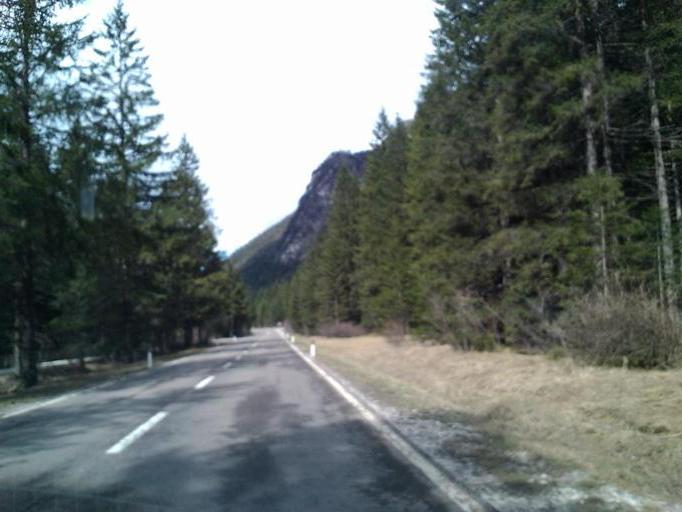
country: IT
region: Trentino-Alto Adige
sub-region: Bolzano
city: Dobbiaco
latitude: 46.6806
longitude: 12.2238
